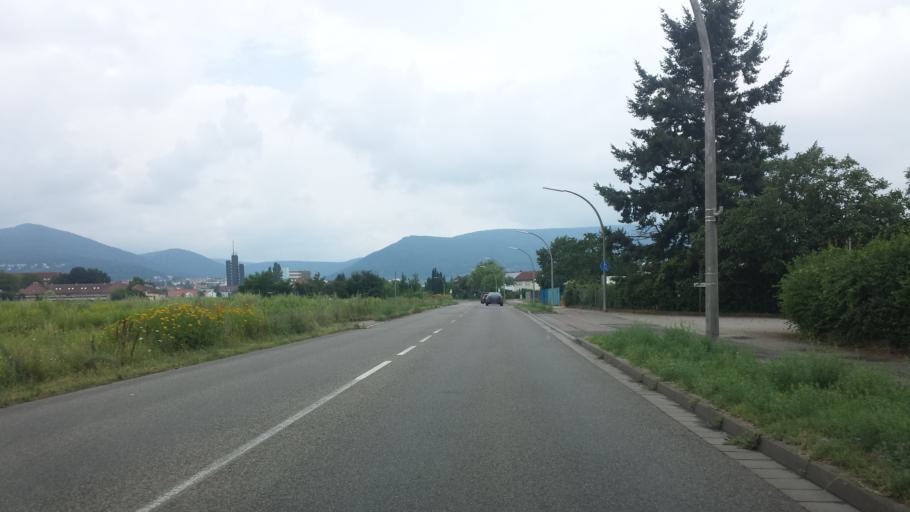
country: DE
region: Rheinland-Pfalz
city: Lachen-Speyerdorf
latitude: 49.3425
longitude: 8.1747
